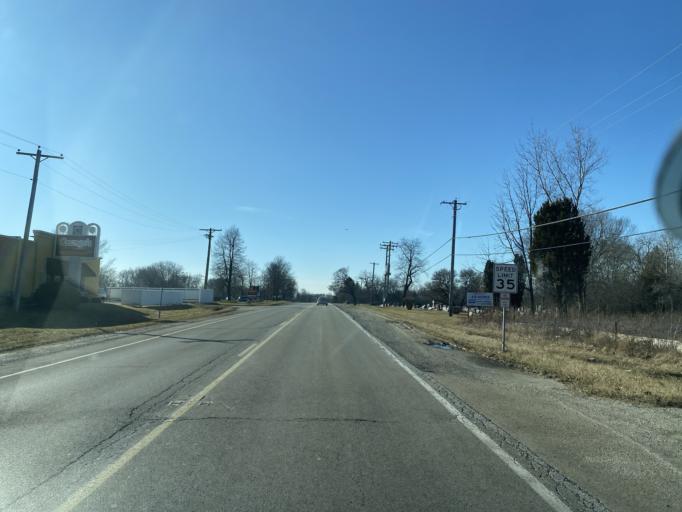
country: US
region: Illinois
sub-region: Will County
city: Lockport
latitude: 41.6099
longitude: -88.0435
